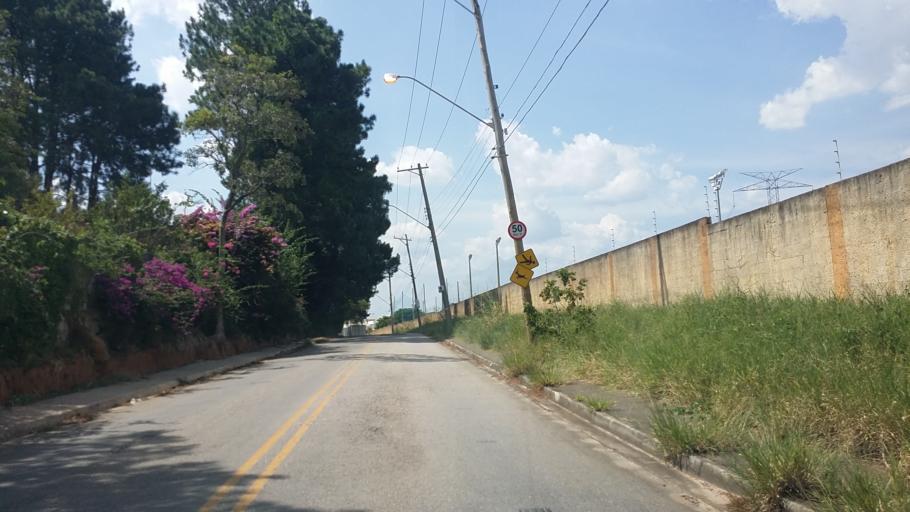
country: BR
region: Sao Paulo
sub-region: Itupeva
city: Itupeva
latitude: -23.2087
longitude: -47.0185
